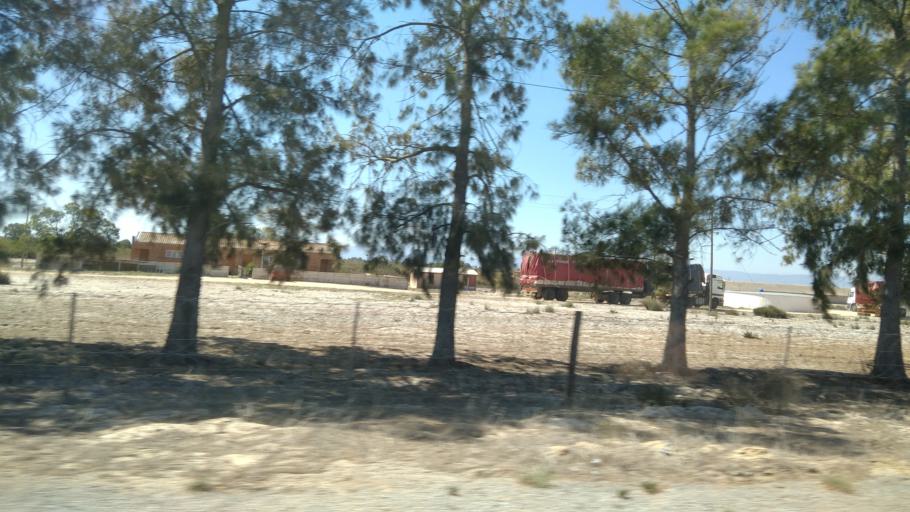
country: ZA
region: Western Cape
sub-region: West Coast District Municipality
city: Vredenburg
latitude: -33.0398
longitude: 18.3080
